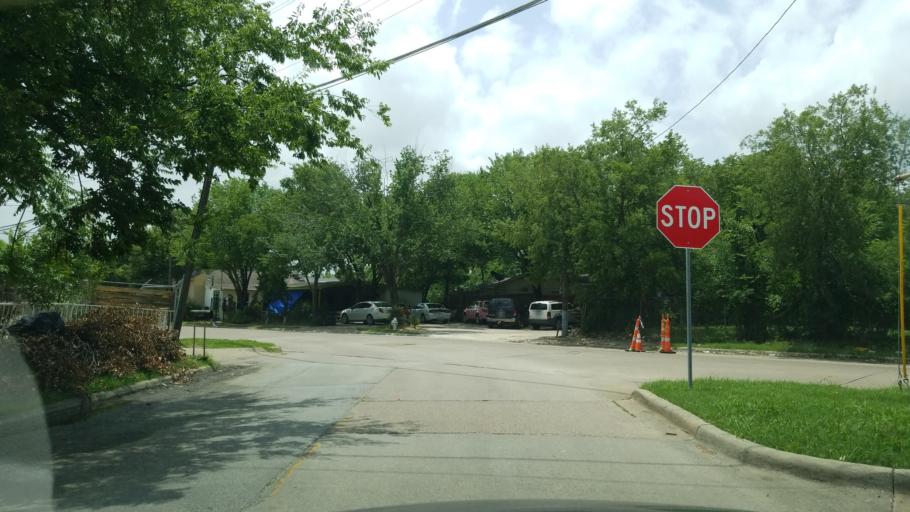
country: US
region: Texas
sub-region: Dallas County
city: Cockrell Hill
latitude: 32.7850
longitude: -96.9003
